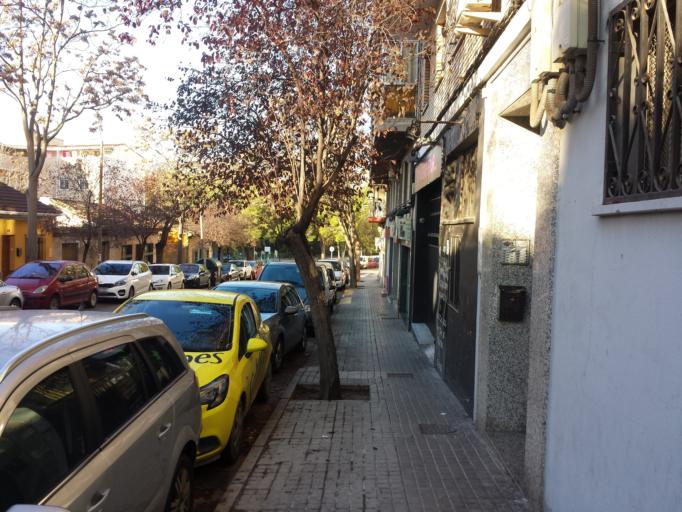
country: ES
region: Aragon
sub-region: Provincia de Zaragoza
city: Delicias
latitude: 41.6293
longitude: -0.8900
